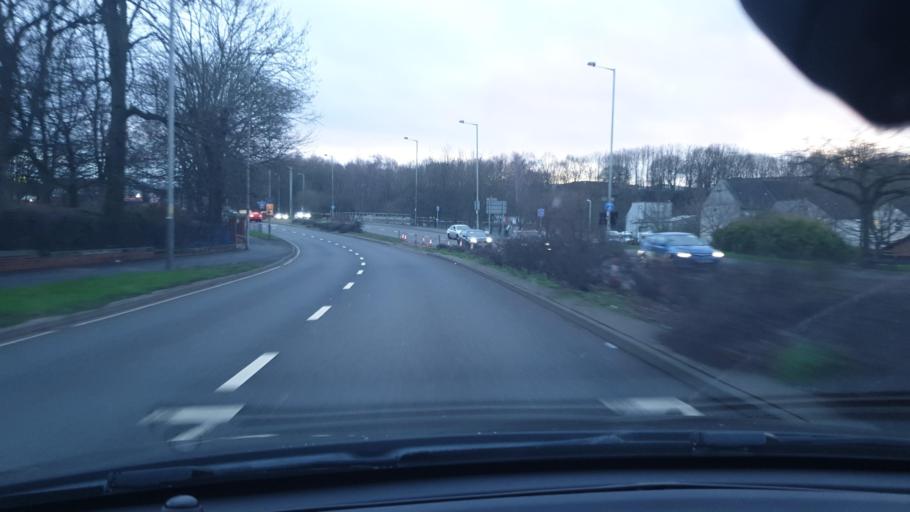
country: GB
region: England
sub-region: Wolverhampton
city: Wolverhampton
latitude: 52.6035
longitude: -2.1303
